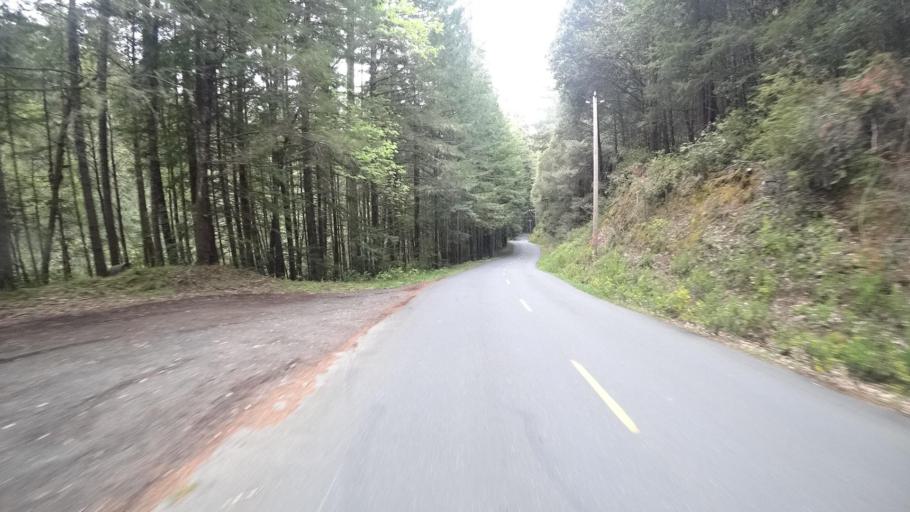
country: US
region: California
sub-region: Humboldt County
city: Redway
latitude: 40.2803
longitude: -123.8497
